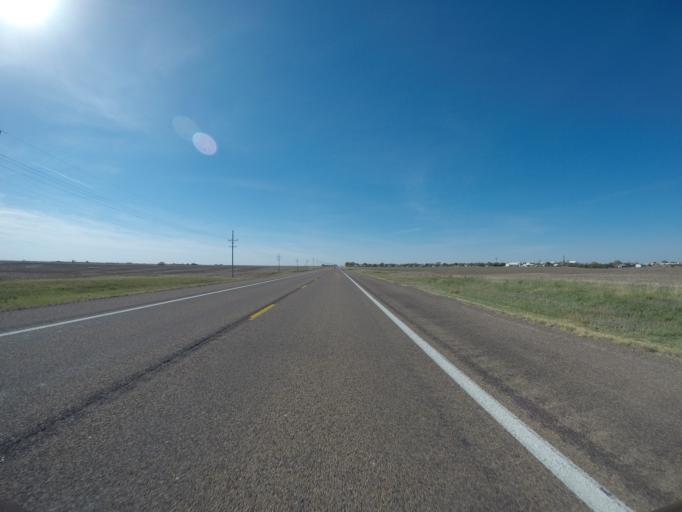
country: US
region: Kansas
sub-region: Phillips County
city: Phillipsburg
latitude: 39.7566
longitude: -99.1049
